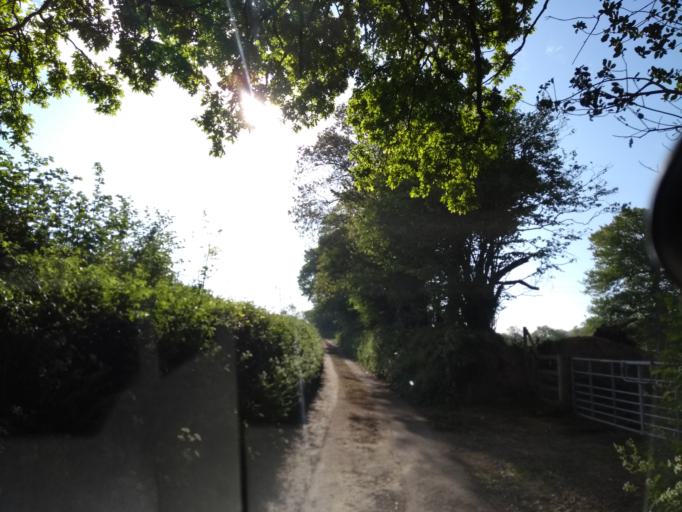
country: GB
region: England
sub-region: Dorset
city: Lyme Regis
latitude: 50.7976
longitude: -2.9050
